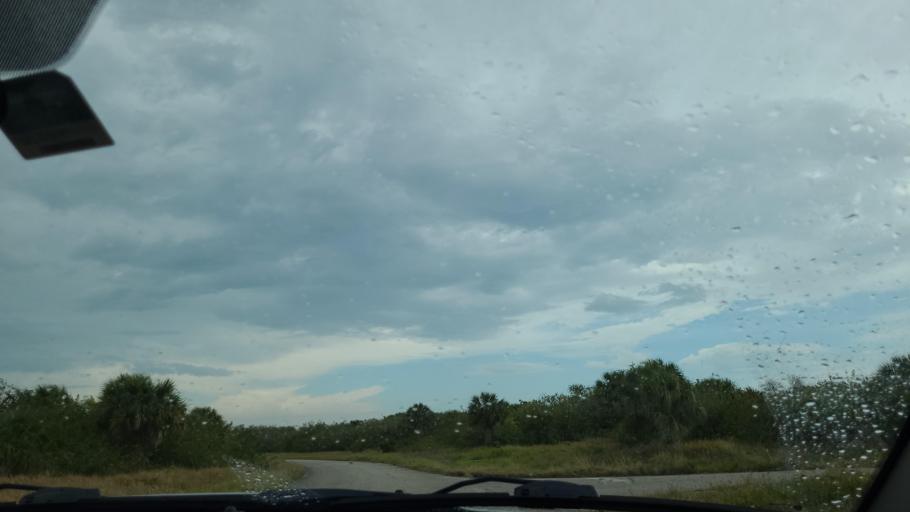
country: US
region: Florida
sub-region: Brevard County
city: June Park
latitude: 27.9436
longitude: -80.7116
